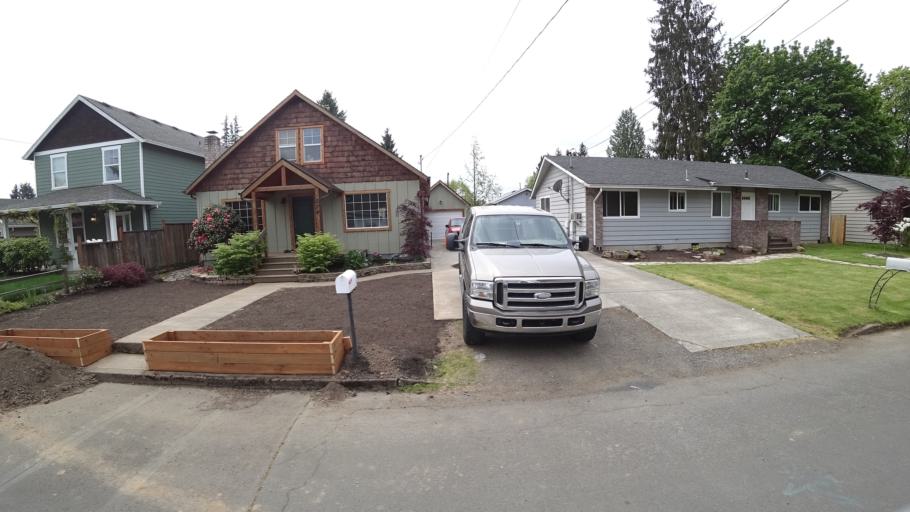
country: US
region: Oregon
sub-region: Washington County
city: Hillsboro
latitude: 45.5287
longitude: -122.9971
